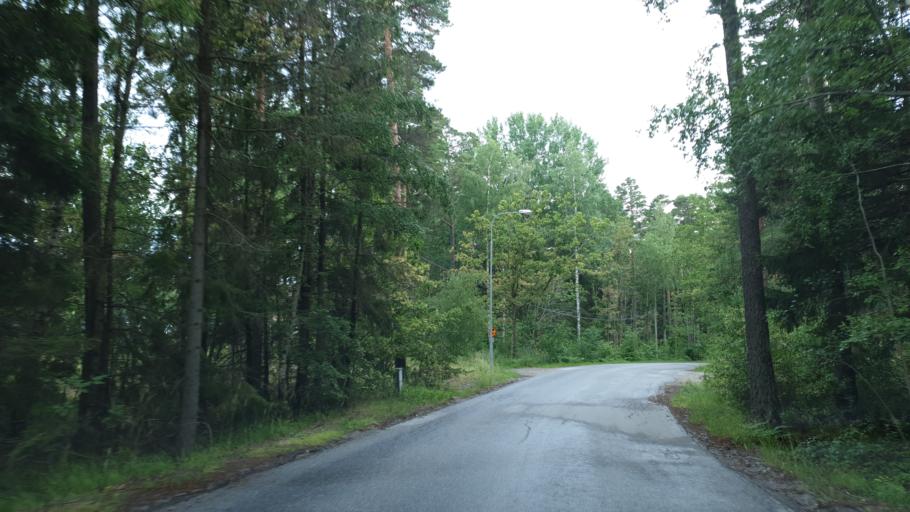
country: SE
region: Stockholm
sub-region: Jarfalla Kommun
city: Jakobsberg
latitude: 59.4267
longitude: 17.8034
